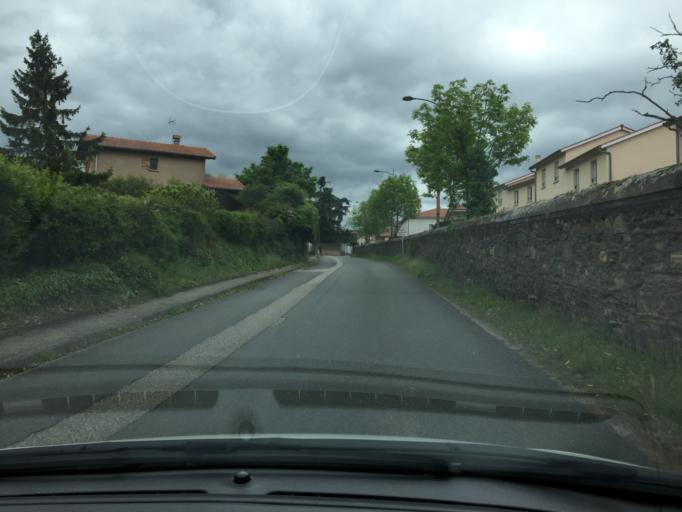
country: FR
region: Rhone-Alpes
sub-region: Departement du Rhone
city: Saint-Maurice-sur-Dargoire
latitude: 45.5852
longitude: 4.6340
